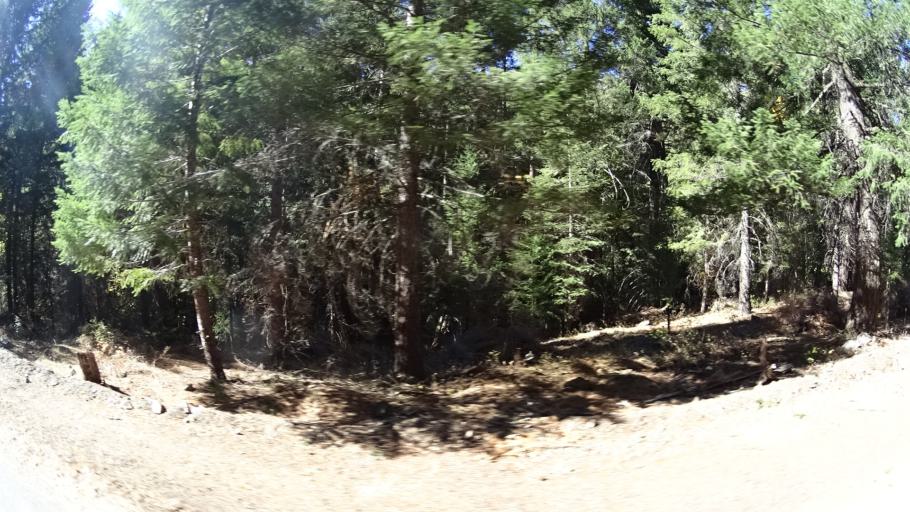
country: US
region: California
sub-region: Siskiyou County
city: Yreka
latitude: 41.3717
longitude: -123.0224
